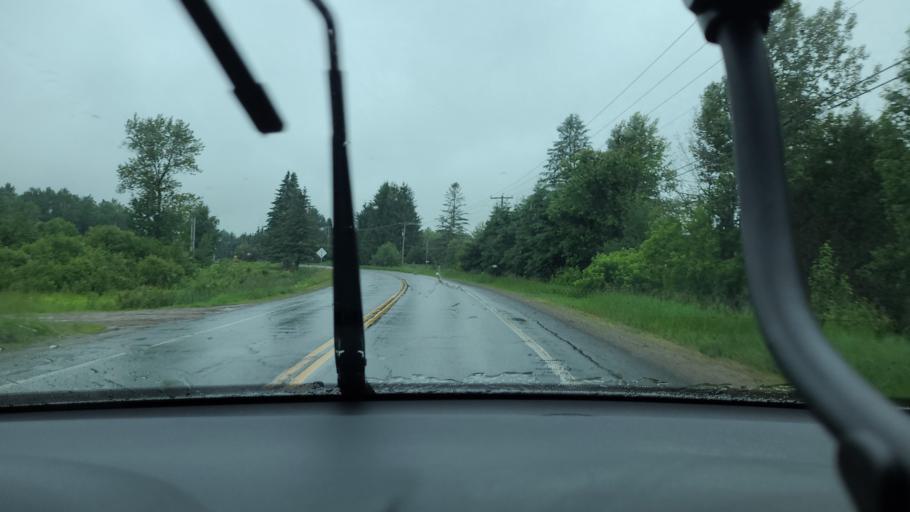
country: CA
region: Quebec
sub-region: Outaouais
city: Saint-Andre-Avellin
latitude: 45.7978
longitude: -75.0666
